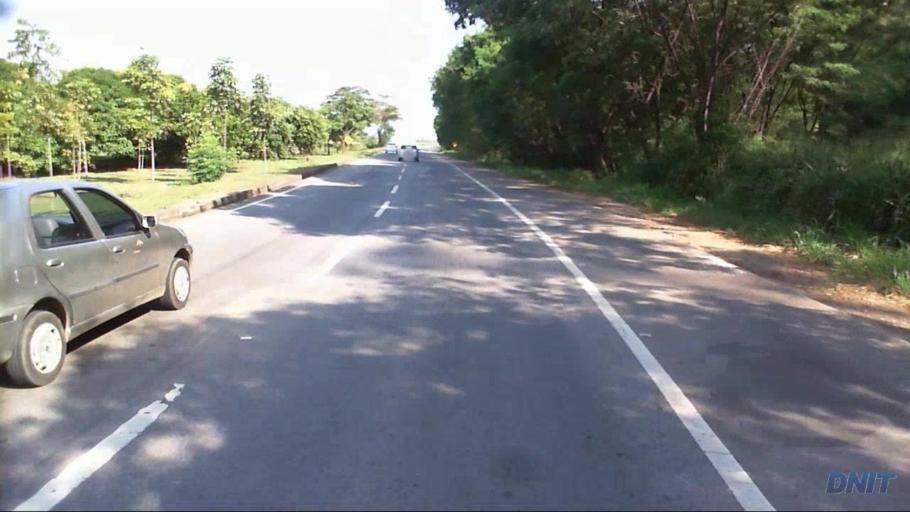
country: BR
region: Minas Gerais
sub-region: Coronel Fabriciano
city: Coronel Fabriciano
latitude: -19.5138
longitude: -42.5763
